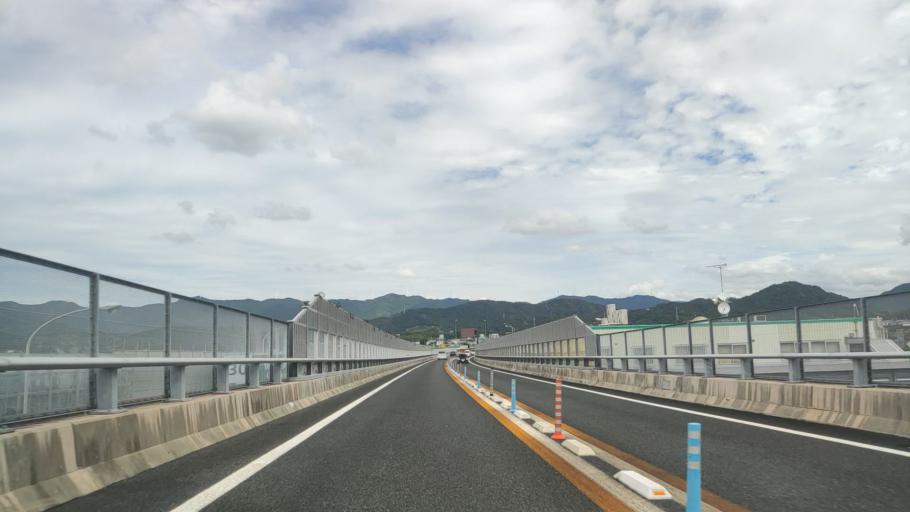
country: JP
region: Wakayama
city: Gobo
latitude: 33.8981
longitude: 135.1847
